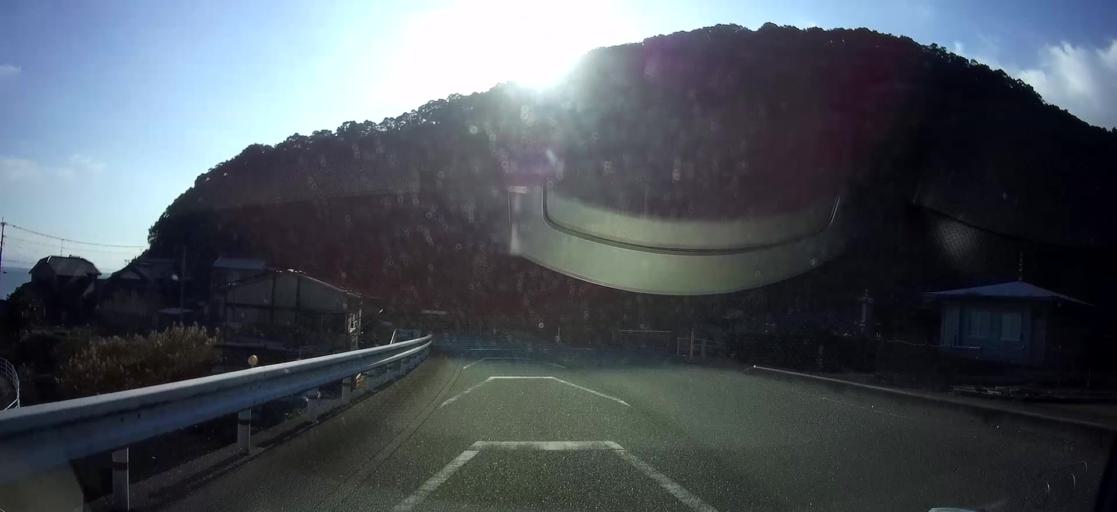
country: JP
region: Kumamoto
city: Minamata
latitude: 32.3919
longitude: 130.3859
